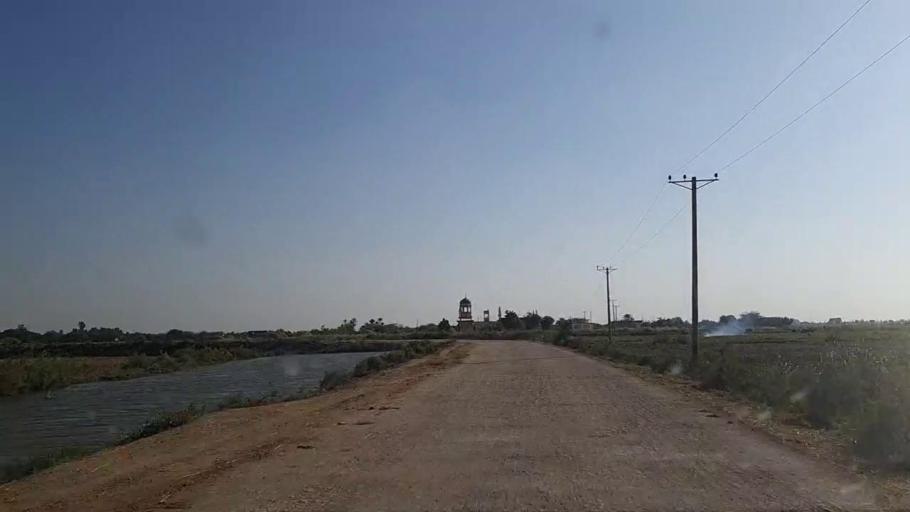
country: PK
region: Sindh
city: Daro Mehar
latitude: 24.6284
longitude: 68.0789
